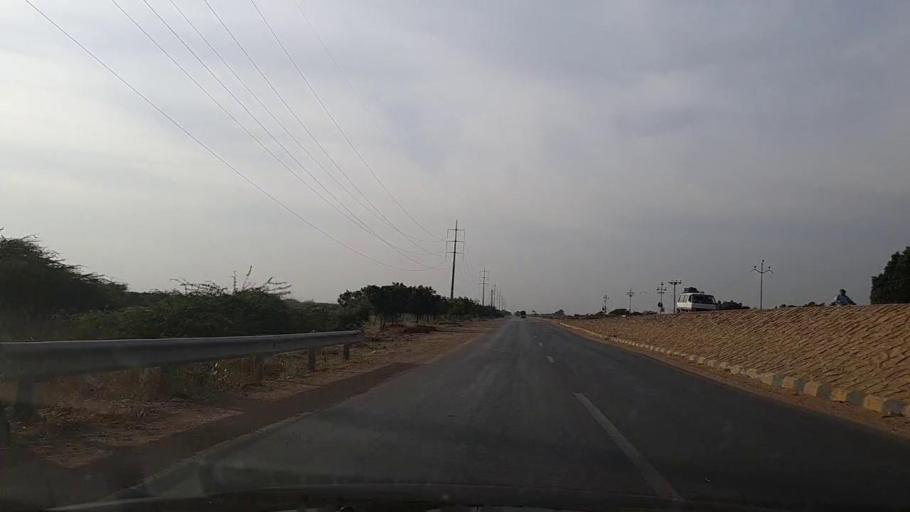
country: PK
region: Sindh
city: Gharo
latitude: 24.8299
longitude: 67.4658
